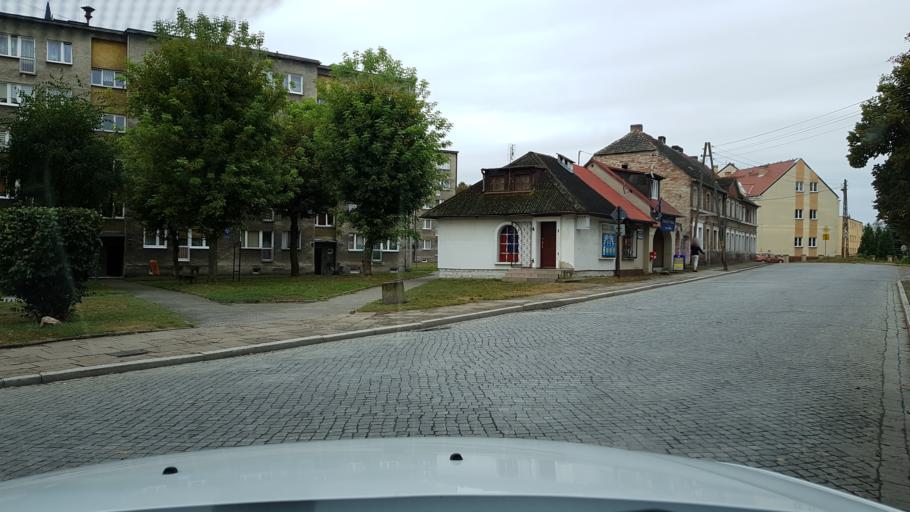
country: PL
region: West Pomeranian Voivodeship
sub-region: Powiat gryfinski
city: Chojna
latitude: 52.9640
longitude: 14.4336
